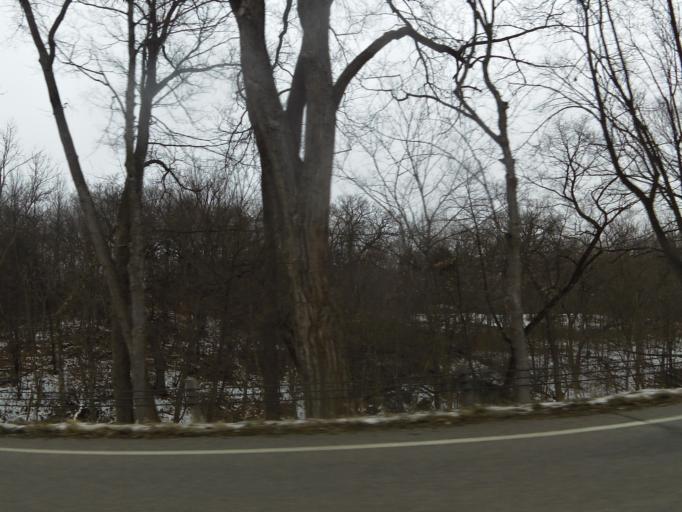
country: US
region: Minnesota
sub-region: Scott County
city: Jordan
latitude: 44.6307
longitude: -93.6020
